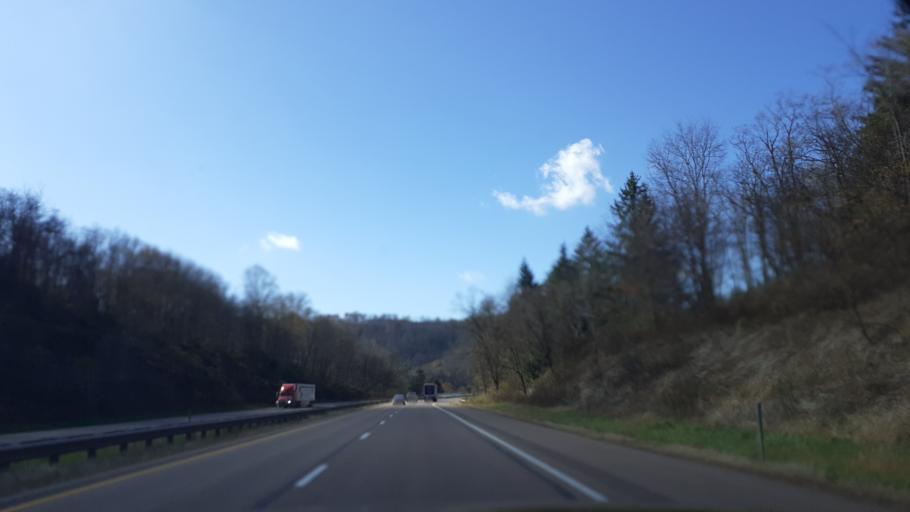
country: US
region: Maryland
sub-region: Garrett County
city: Oakland
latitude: 39.6613
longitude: -79.4023
